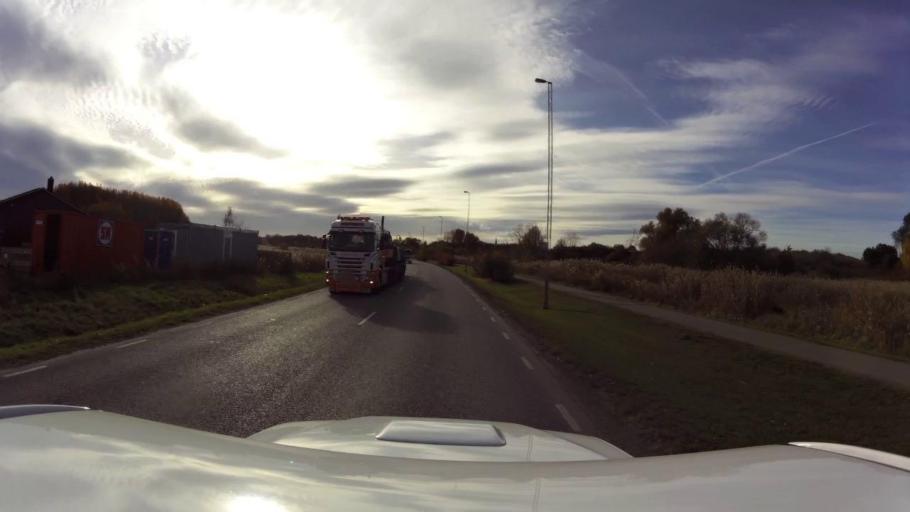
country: SE
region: OEstergoetland
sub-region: Linkopings Kommun
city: Linkoping
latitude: 58.4290
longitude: 15.6396
